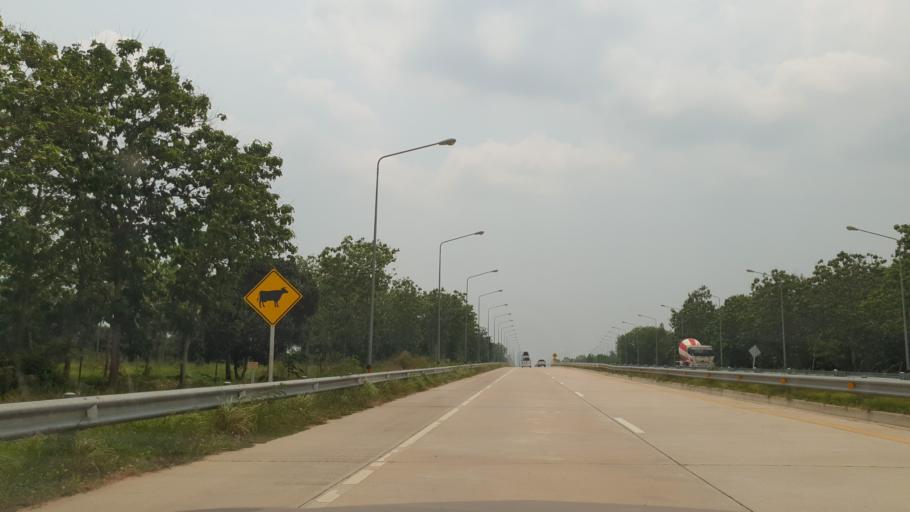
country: TH
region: Chon Buri
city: Phatthaya
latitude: 12.8400
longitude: 100.9532
